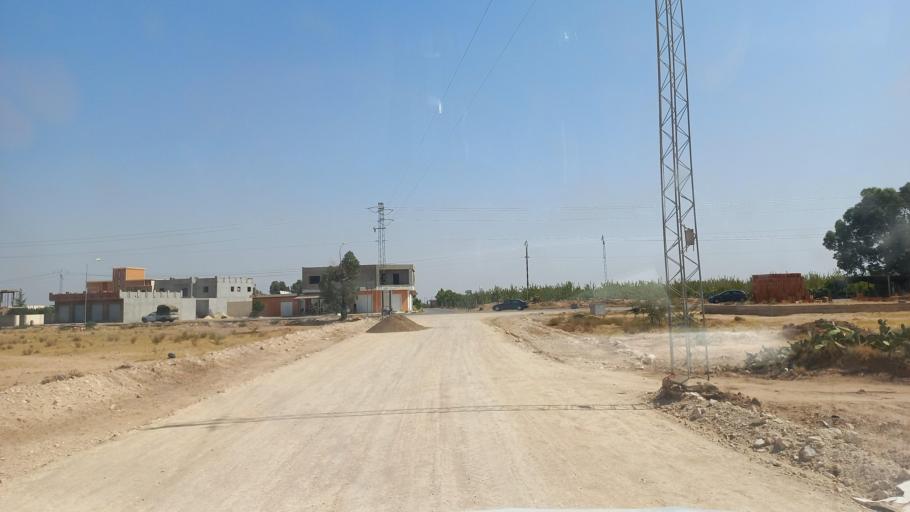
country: TN
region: Al Qasrayn
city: Kasserine
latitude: 35.2545
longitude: 9.0162
